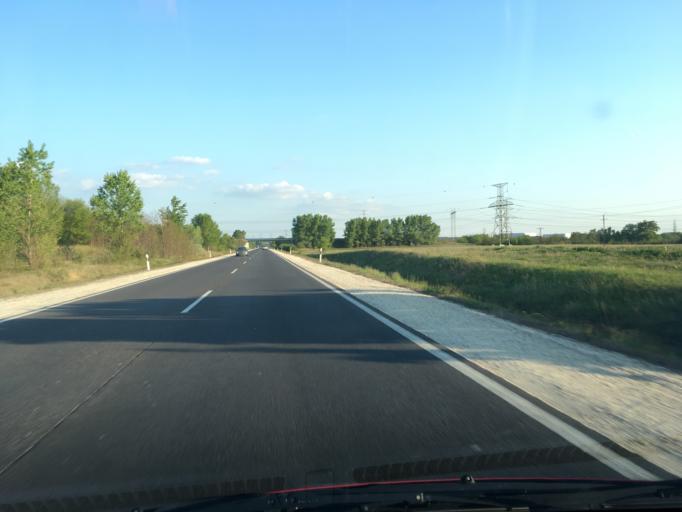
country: HU
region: Pest
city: Szod
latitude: 47.6991
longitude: 19.1691
